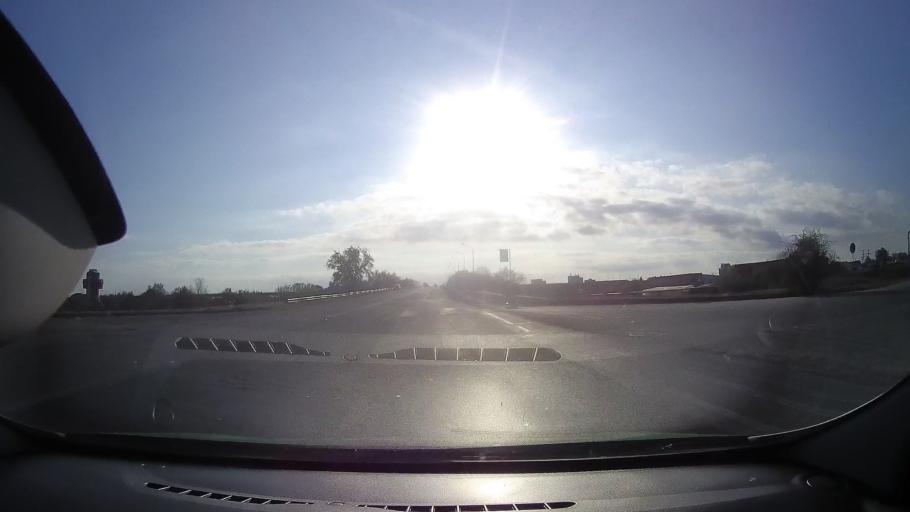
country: RO
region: Constanta
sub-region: Comuna Navodari
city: Navodari
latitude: 44.3257
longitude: 28.6249
